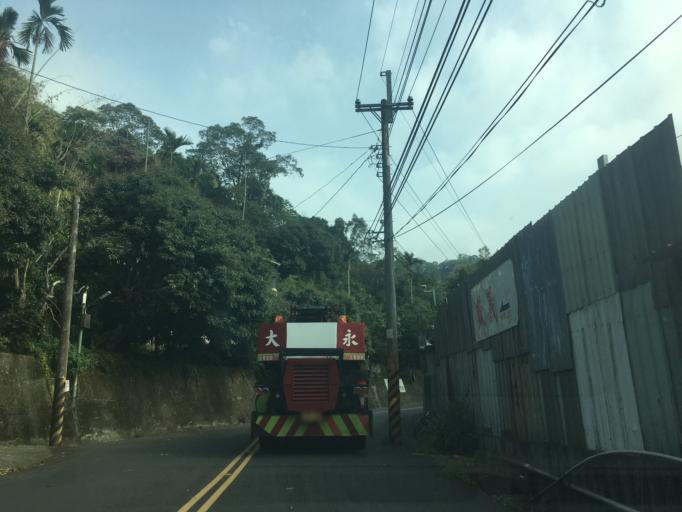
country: TW
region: Taiwan
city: Fengyuan
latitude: 24.2293
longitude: 120.7531
